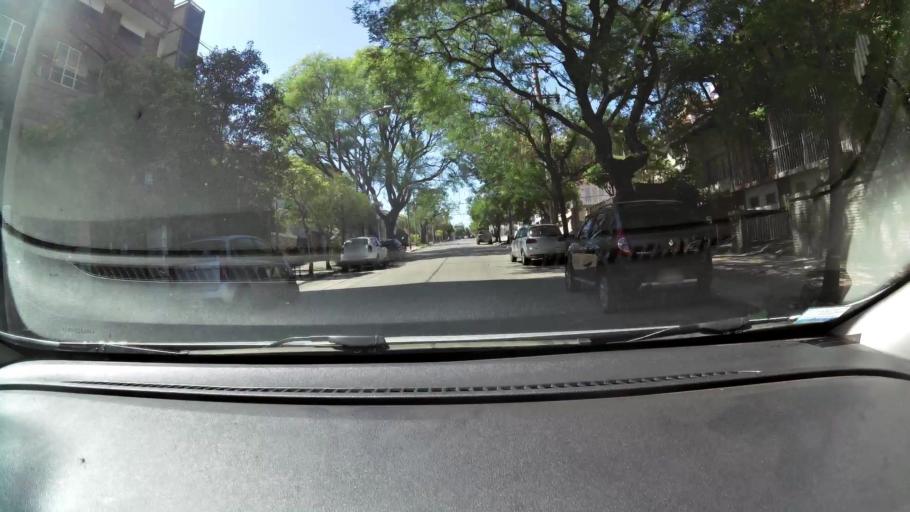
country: AR
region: Cordoba
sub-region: Departamento de Capital
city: Cordoba
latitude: -31.4035
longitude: -64.1874
